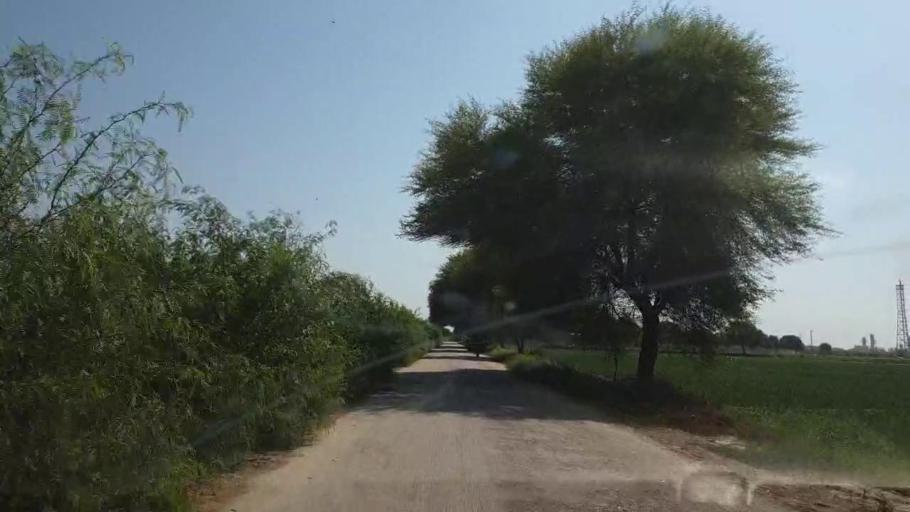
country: PK
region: Sindh
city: Tando Jam
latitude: 25.3940
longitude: 68.5870
